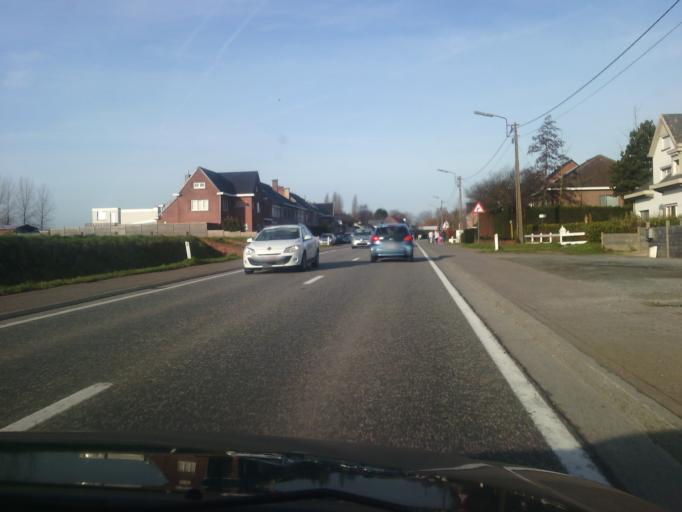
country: BE
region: Flanders
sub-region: Provincie Oost-Vlaanderen
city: Lede
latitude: 50.9550
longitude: 3.9797
